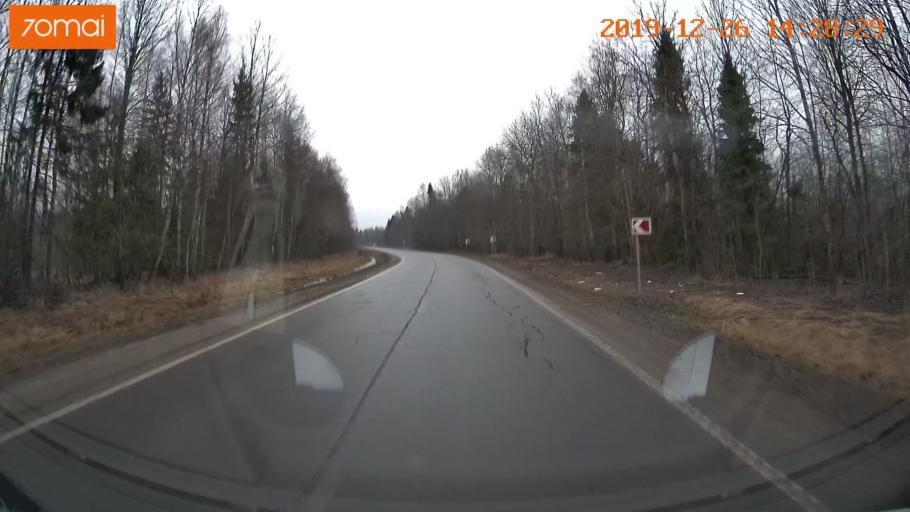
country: RU
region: Jaroslavl
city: Poshekhon'ye
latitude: 58.4751
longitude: 39.0528
